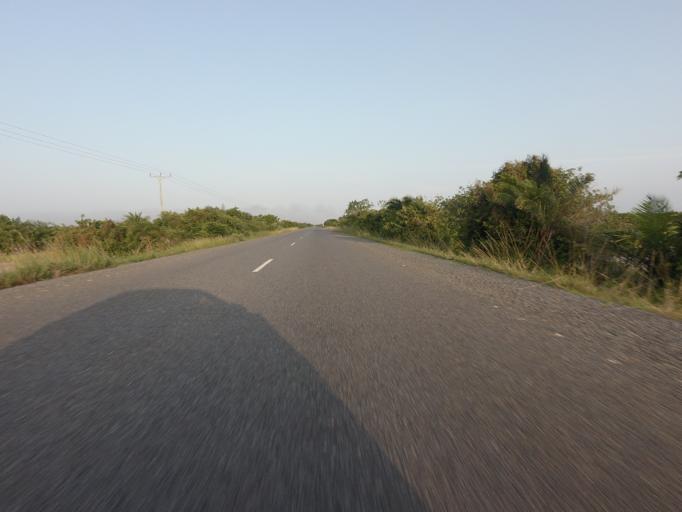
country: GH
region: Volta
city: Anloga
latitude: 5.8491
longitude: 0.7754
